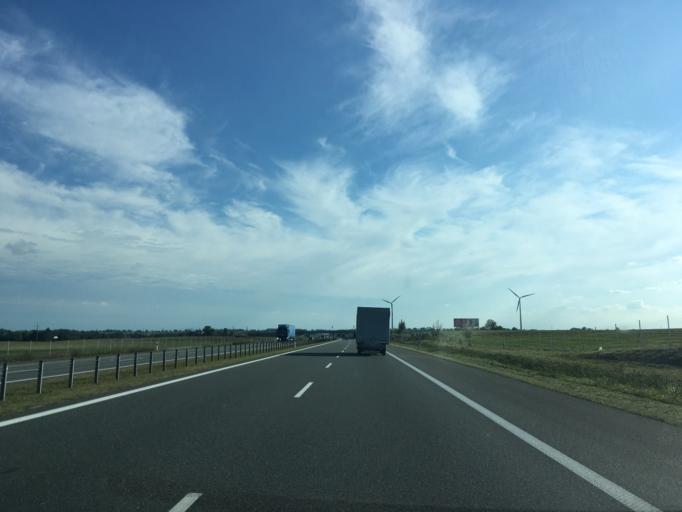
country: PL
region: Kujawsko-Pomorskie
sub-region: Powiat chelminski
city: Lisewo
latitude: 53.3761
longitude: 18.6907
